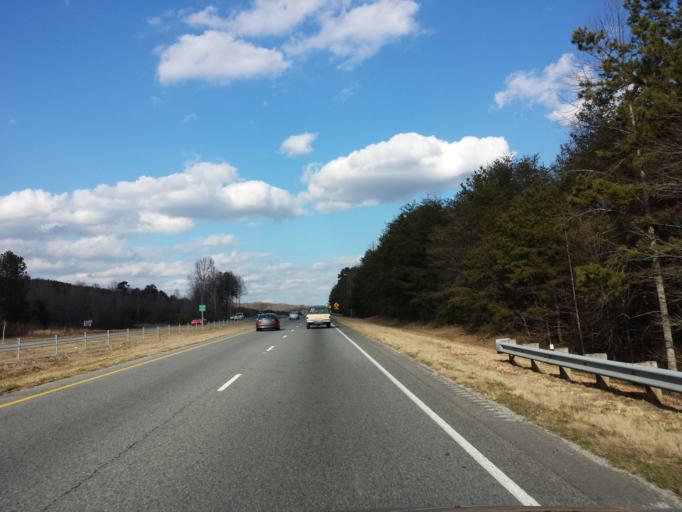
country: US
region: Georgia
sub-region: Lumpkin County
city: Dahlonega
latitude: 34.4556
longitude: -83.9764
